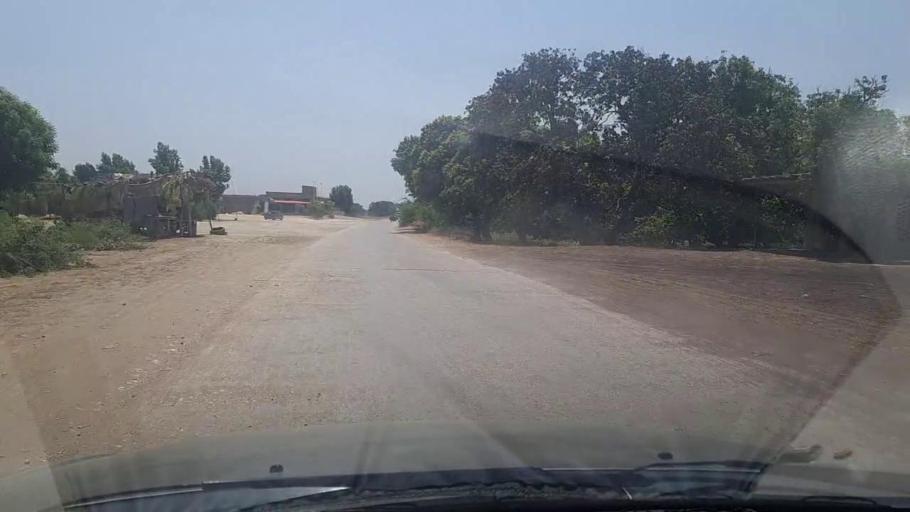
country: PK
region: Sindh
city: Tando Jam
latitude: 25.3006
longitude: 68.5837
